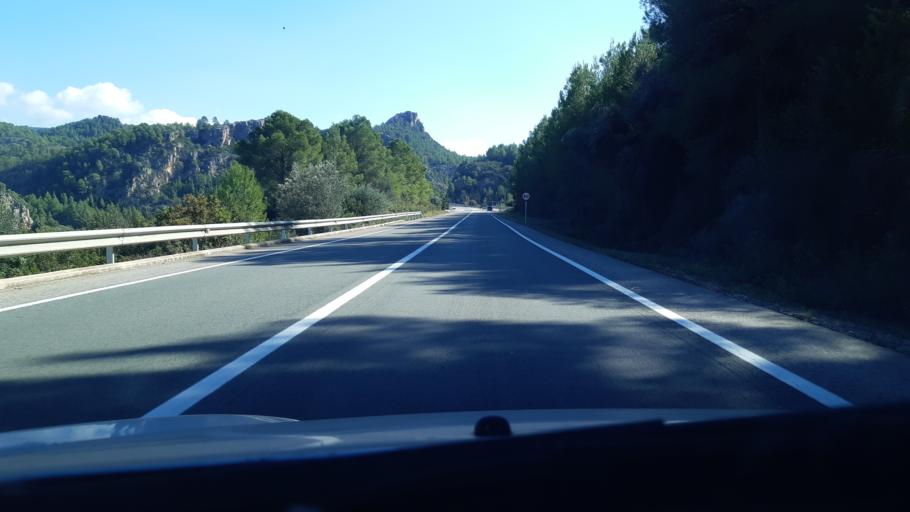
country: ES
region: Catalonia
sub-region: Provincia de Tarragona
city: Benifallet
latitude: 40.9447
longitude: 0.4845
